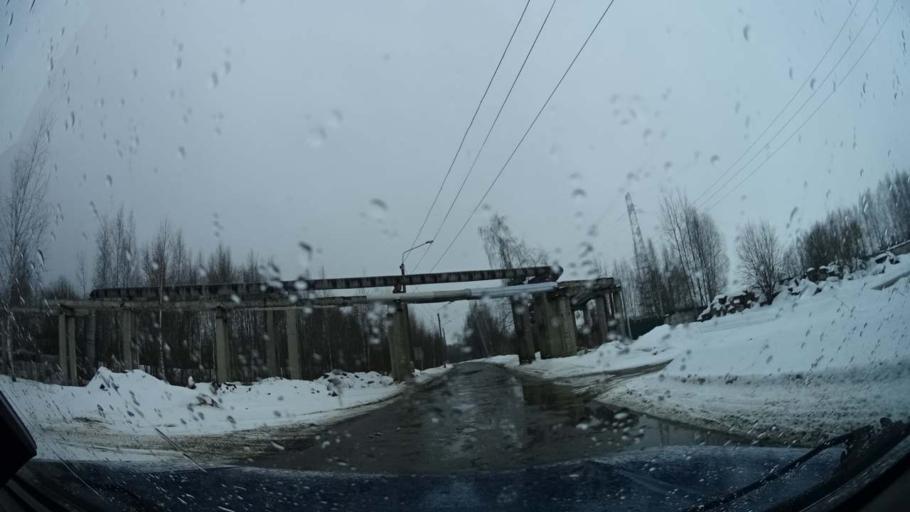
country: RU
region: Tverskaya
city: Konakovo
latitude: 56.7329
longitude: 36.7762
